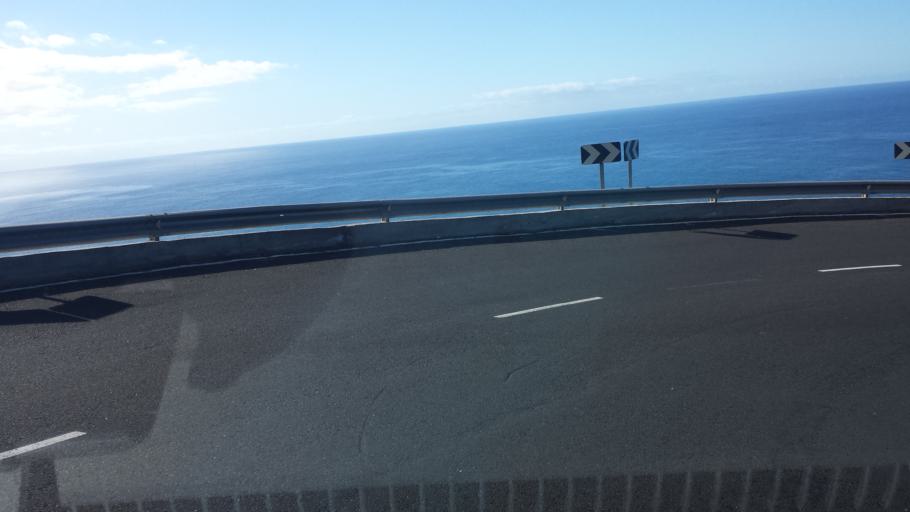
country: ES
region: Canary Islands
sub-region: Provincia de Santa Cruz de Tenerife
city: Tazacorte
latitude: 28.5917
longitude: -17.9103
